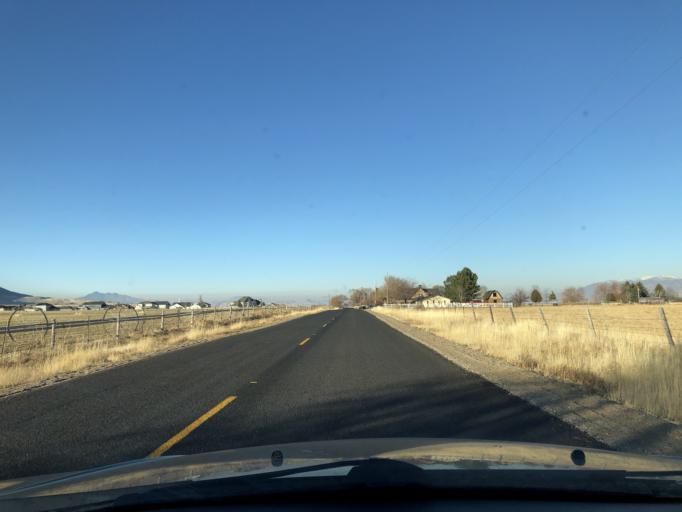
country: US
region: Utah
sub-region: Cache County
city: Wellsville
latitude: 41.6035
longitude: -111.9298
